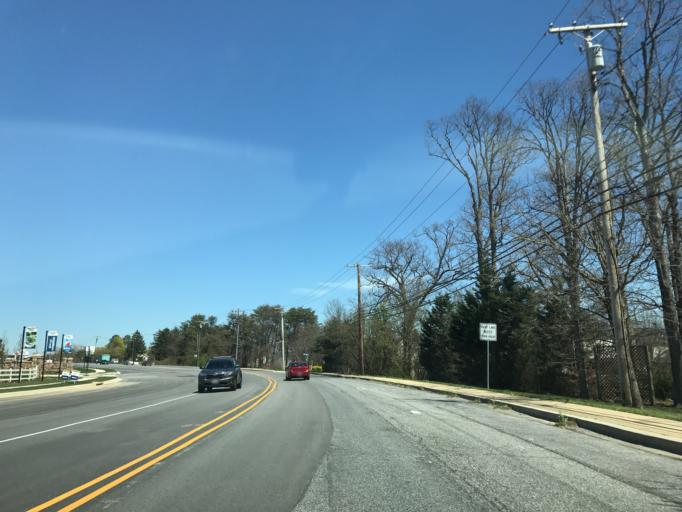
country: US
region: Maryland
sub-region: Anne Arundel County
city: Fort Meade
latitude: 39.1326
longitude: -76.7358
